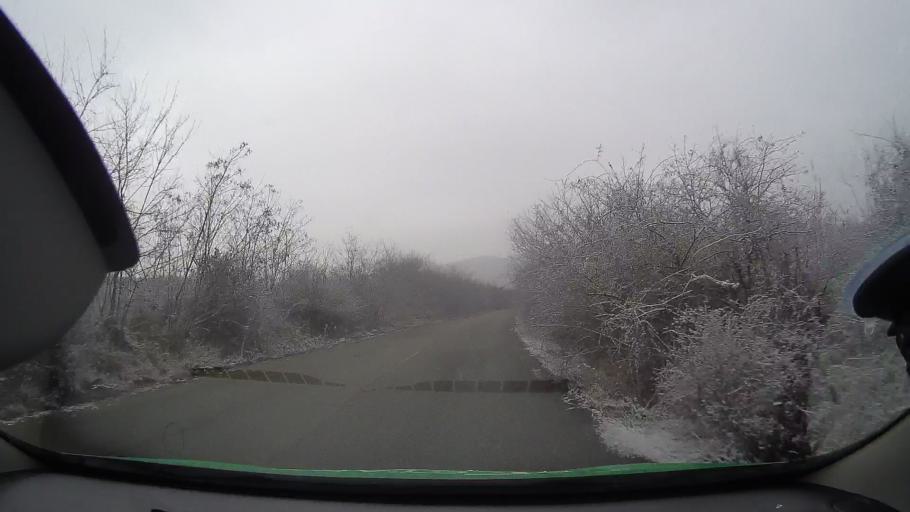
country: RO
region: Alba
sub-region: Comuna Hoparta
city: Hoparta
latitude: 46.3419
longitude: 23.9248
